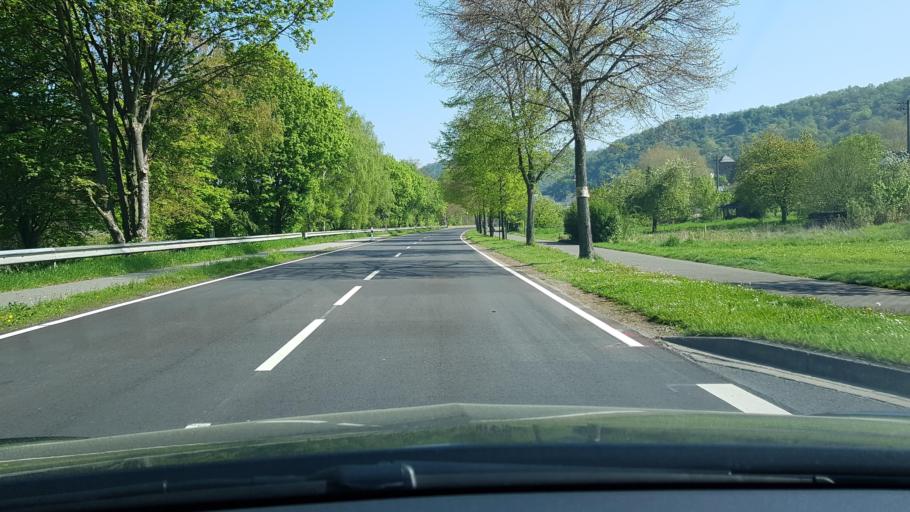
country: DE
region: Rheinland-Pfalz
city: Niederfell
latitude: 50.2876
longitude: 7.4586
